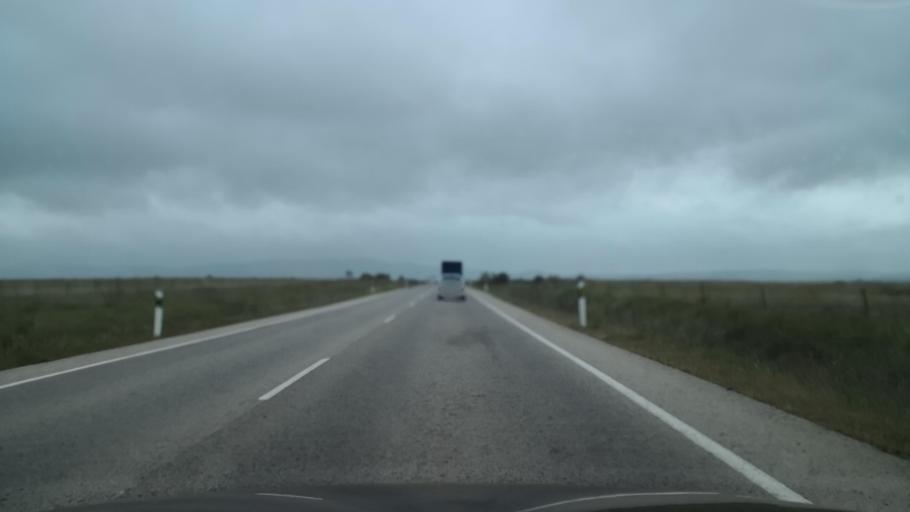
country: ES
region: Extremadura
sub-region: Provincia de Caceres
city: Malpartida de Caceres
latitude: 39.3515
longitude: -6.4690
